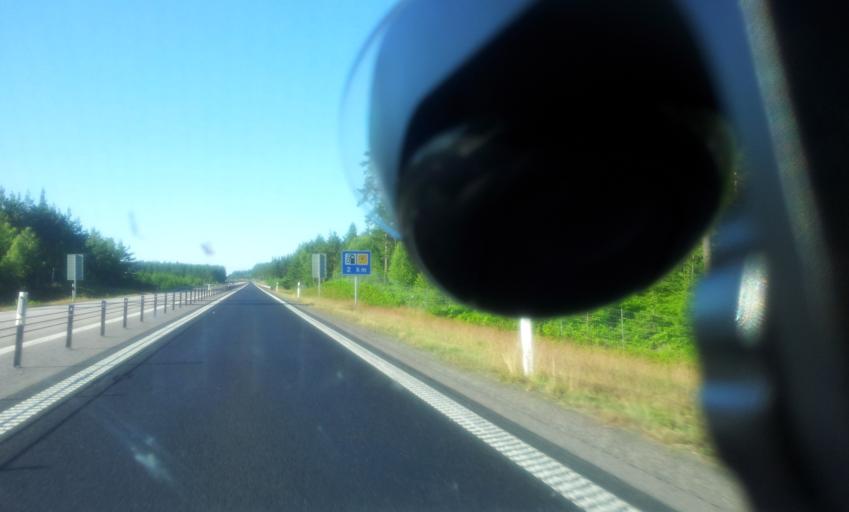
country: SE
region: Kalmar
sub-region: Torsas Kommun
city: Torsas
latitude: 56.4745
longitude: 16.0800
